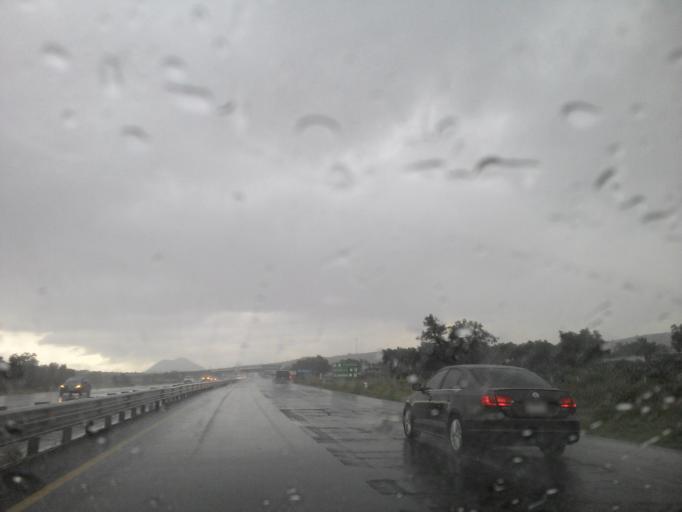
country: MX
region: Hidalgo
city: Zempoala
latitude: 19.8746
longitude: -98.6673
